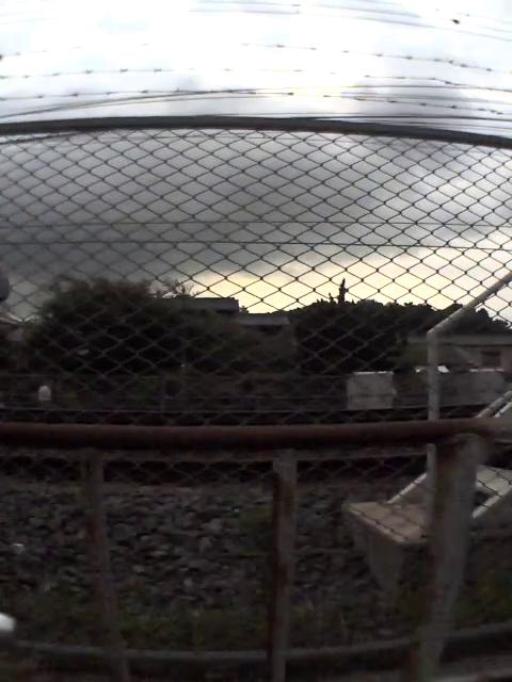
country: JP
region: Osaka
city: Hirakata
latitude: 34.8303
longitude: 135.6544
